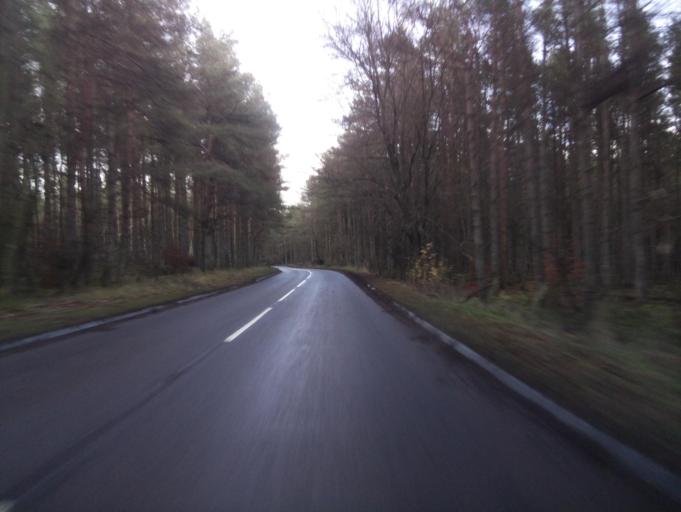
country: GB
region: Scotland
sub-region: Angus
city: Letham
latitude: 56.5849
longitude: -2.8331
